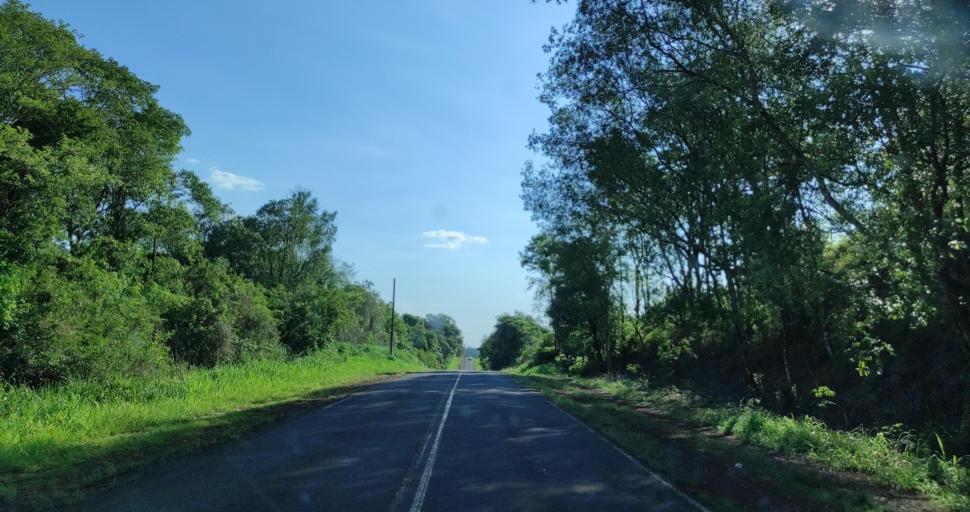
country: AR
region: Misiones
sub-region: Departamento de Eldorado
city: Eldorado
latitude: -26.3905
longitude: -54.3579
